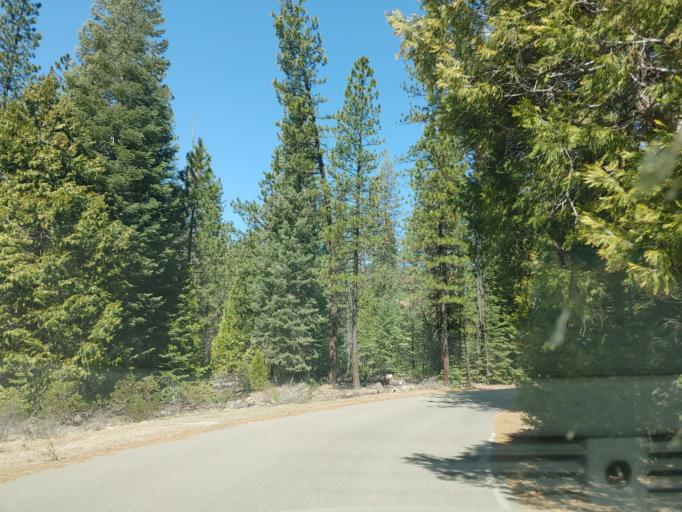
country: US
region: California
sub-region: Siskiyou County
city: McCloud
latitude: 41.2372
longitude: -122.0088
